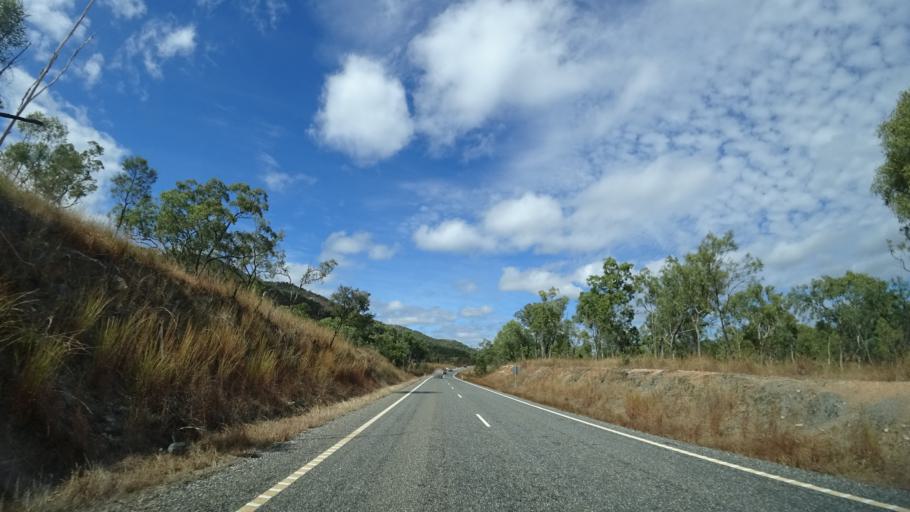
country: AU
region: Queensland
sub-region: Cairns
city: Port Douglas
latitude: -16.3365
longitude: 144.7242
